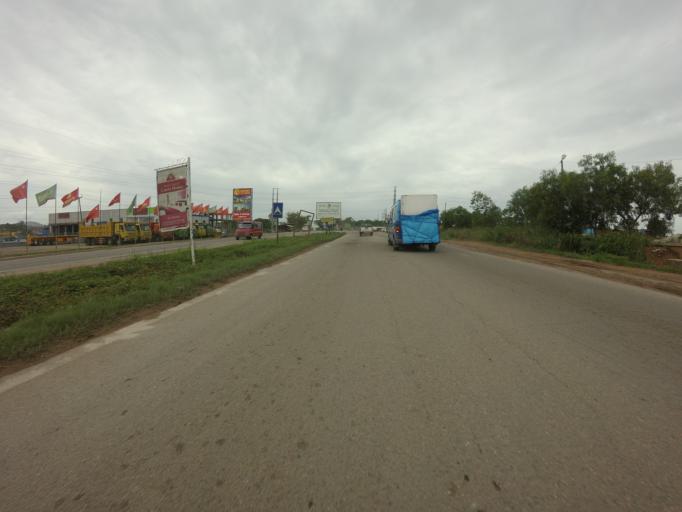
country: GH
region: Eastern
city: Nsawam
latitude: 5.7900
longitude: -0.3381
